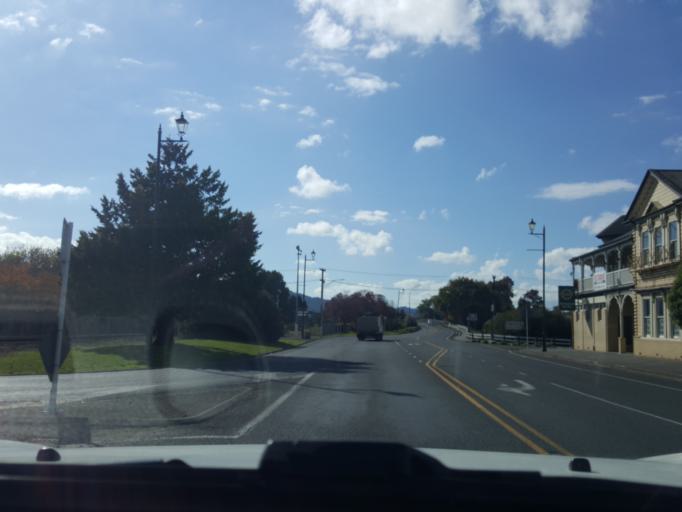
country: NZ
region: Waikato
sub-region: Waikato District
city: Ngaruawahia
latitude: -37.6650
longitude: 175.1479
